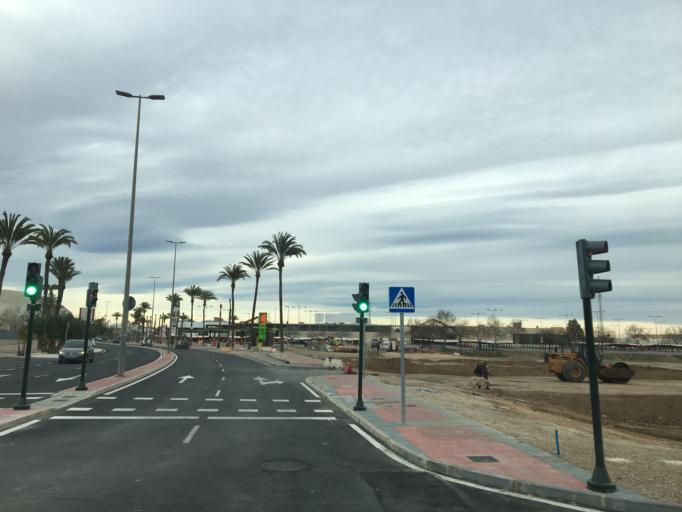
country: ES
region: Murcia
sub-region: Murcia
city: Cartagena
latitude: 37.6114
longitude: -1.0037
